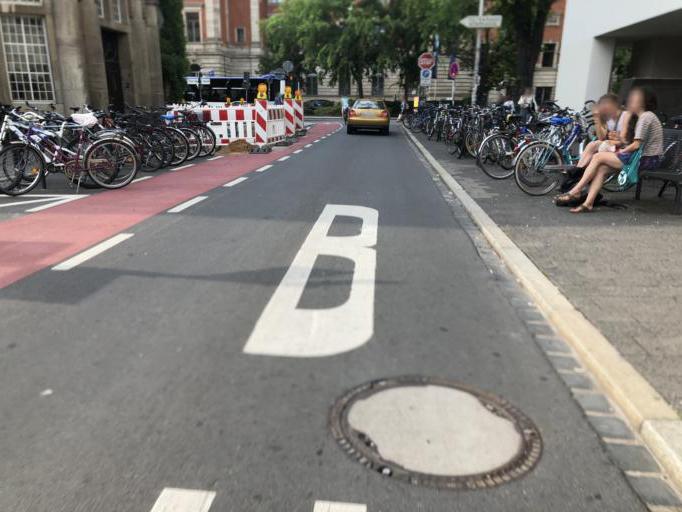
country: DE
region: Bavaria
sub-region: Regierungsbezirk Mittelfranken
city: Erlangen
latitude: 49.5965
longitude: 11.0072
